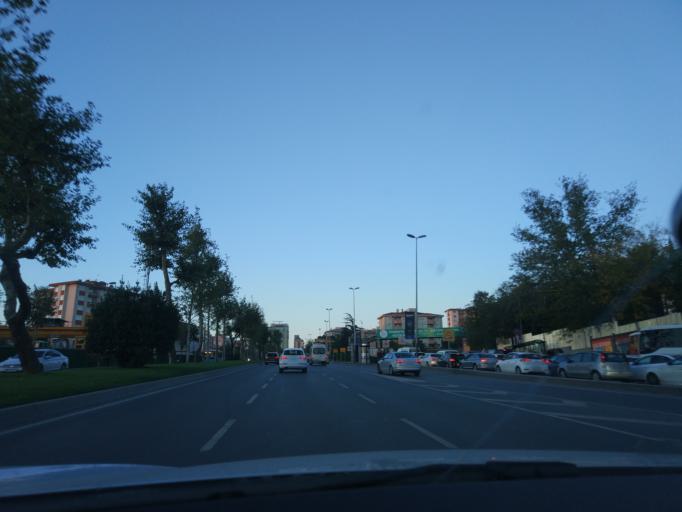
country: TR
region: Istanbul
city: Sisli
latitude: 41.0523
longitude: 29.0090
